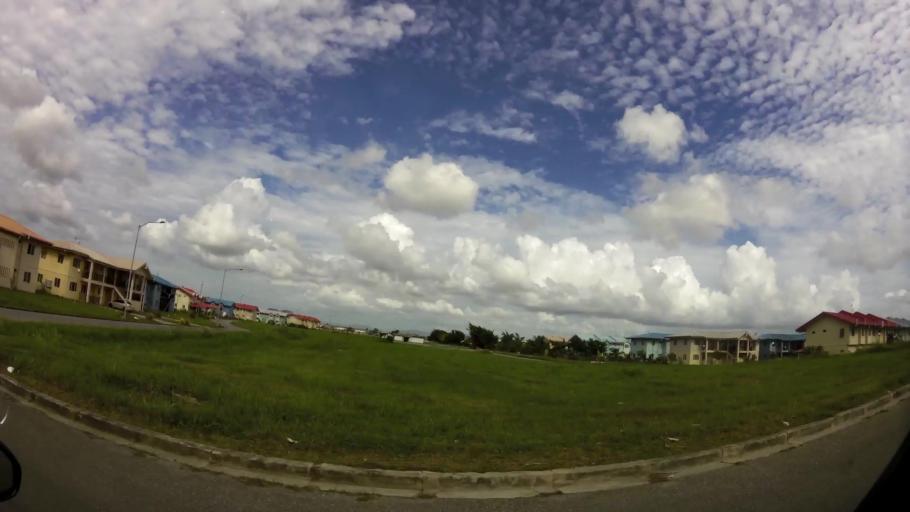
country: TT
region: Chaguanas
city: Chaguanas
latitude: 10.5022
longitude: -61.3945
